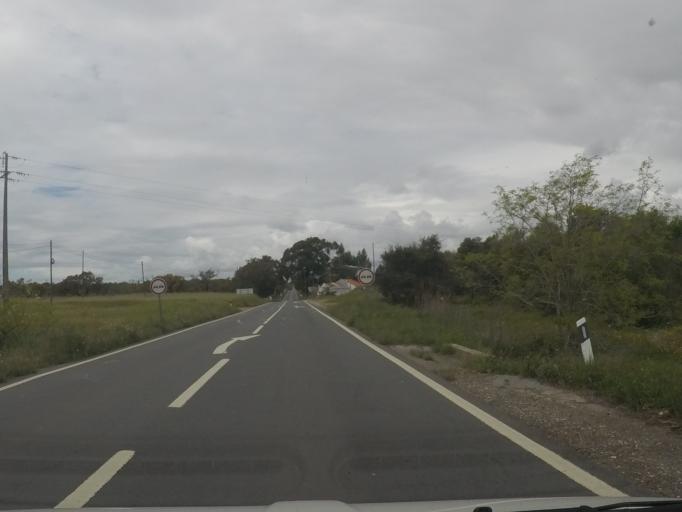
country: PT
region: Setubal
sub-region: Santiago do Cacem
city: Cercal
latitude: 37.8500
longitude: -8.7098
